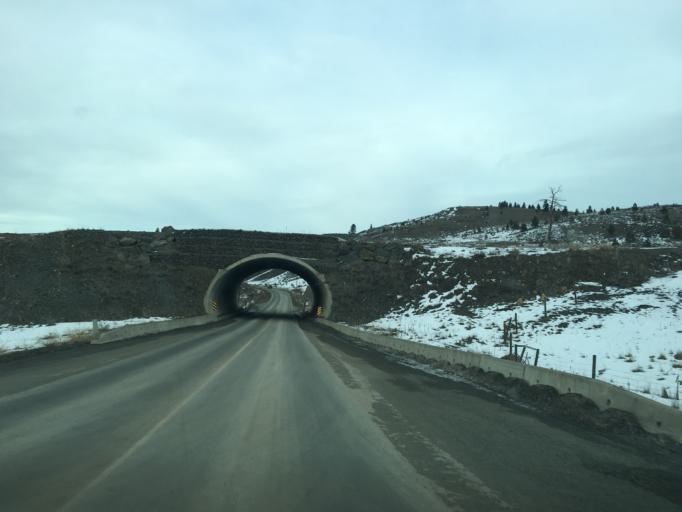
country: CA
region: British Columbia
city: Kamloops
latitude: 50.6165
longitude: -120.4437
